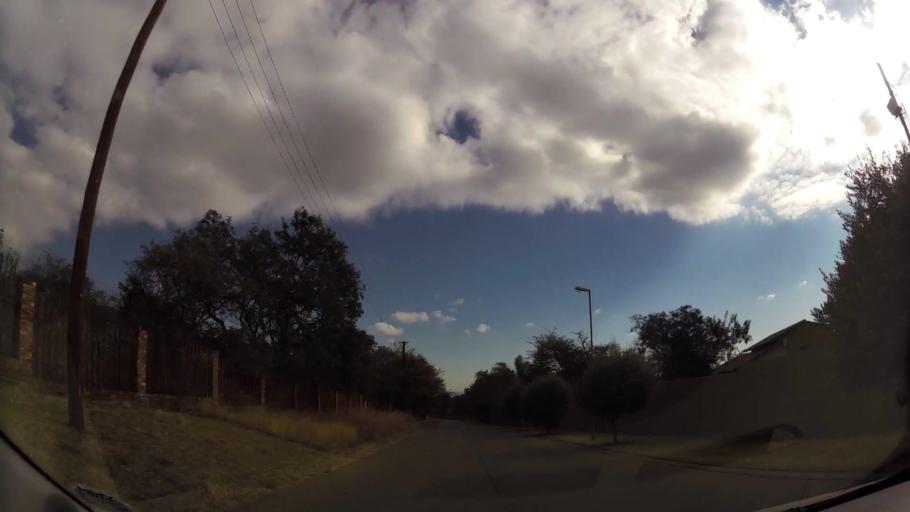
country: ZA
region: Gauteng
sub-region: City of Johannesburg Metropolitan Municipality
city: Roodepoort
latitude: -26.1008
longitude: 27.8709
